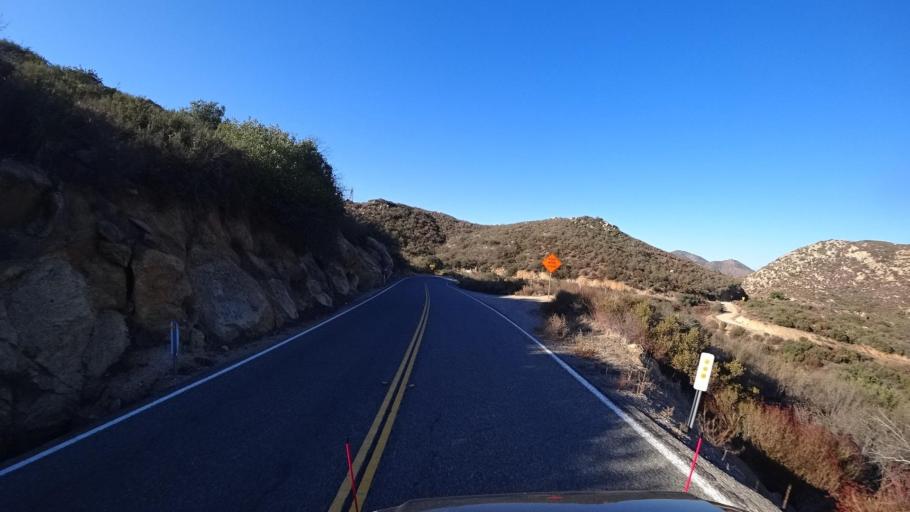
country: MX
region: Baja California
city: Tecate
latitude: 32.6014
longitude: -116.6392
